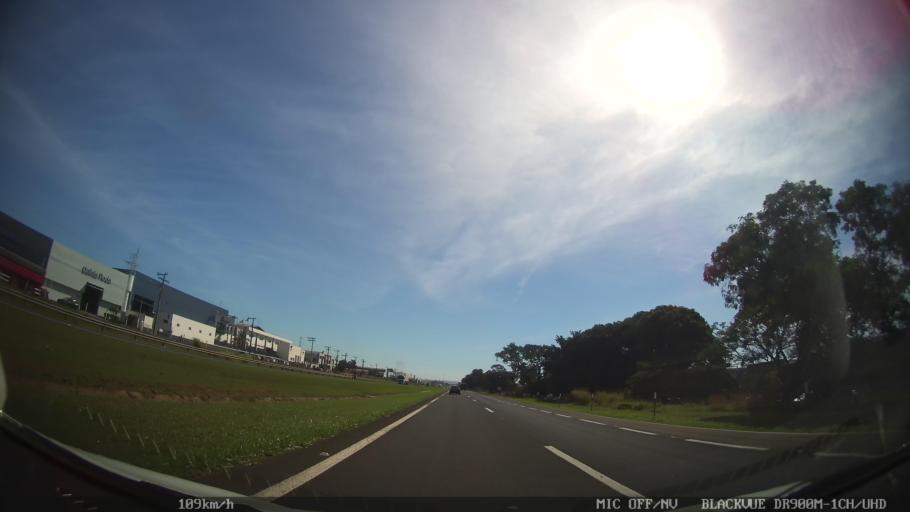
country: BR
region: Sao Paulo
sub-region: Porto Ferreira
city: Porto Ferreira
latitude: -21.8792
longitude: -47.4862
